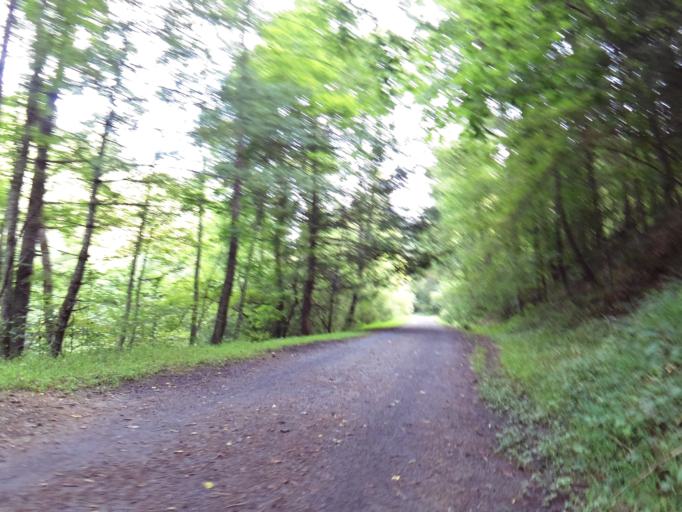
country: US
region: Virginia
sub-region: Washington County
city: Abingdon
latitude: 36.6936
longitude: -81.9406
